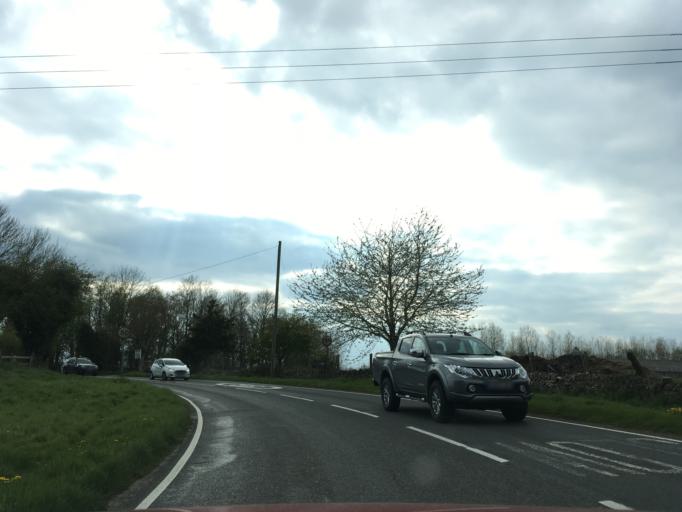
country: GB
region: England
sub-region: Oxfordshire
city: Kidlington
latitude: 51.8706
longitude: -1.2790
